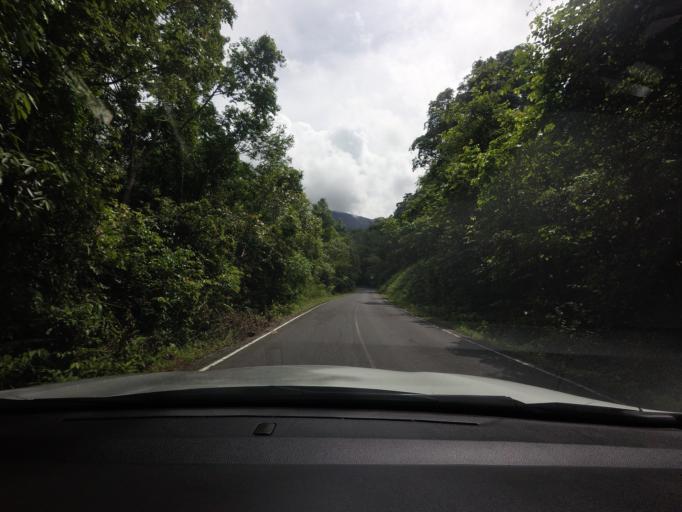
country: TH
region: Nakhon Nayok
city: Pak Phli
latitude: 14.3326
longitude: 101.3582
